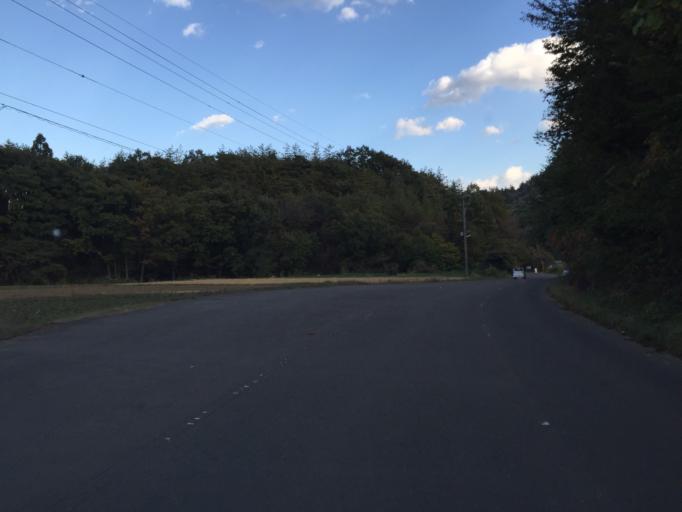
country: JP
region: Fukushima
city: Fukushima-shi
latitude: 37.7054
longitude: 140.4040
